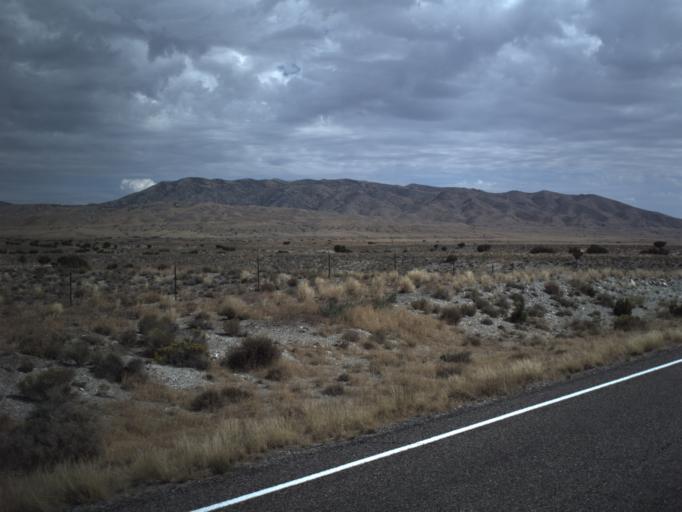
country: US
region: Utah
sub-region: Tooele County
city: Wendover
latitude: 41.4341
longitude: -113.7694
